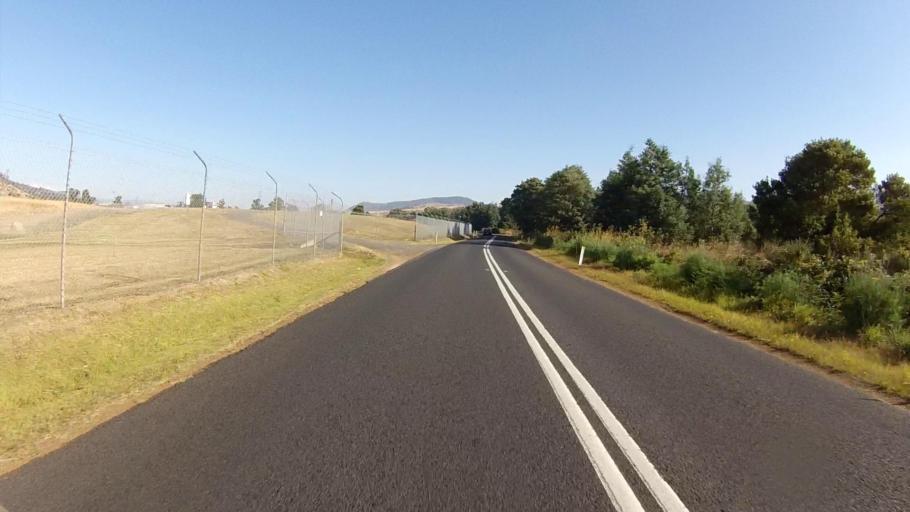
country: AU
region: Tasmania
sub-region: Derwent Valley
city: New Norfolk
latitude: -42.7706
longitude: 147.0266
